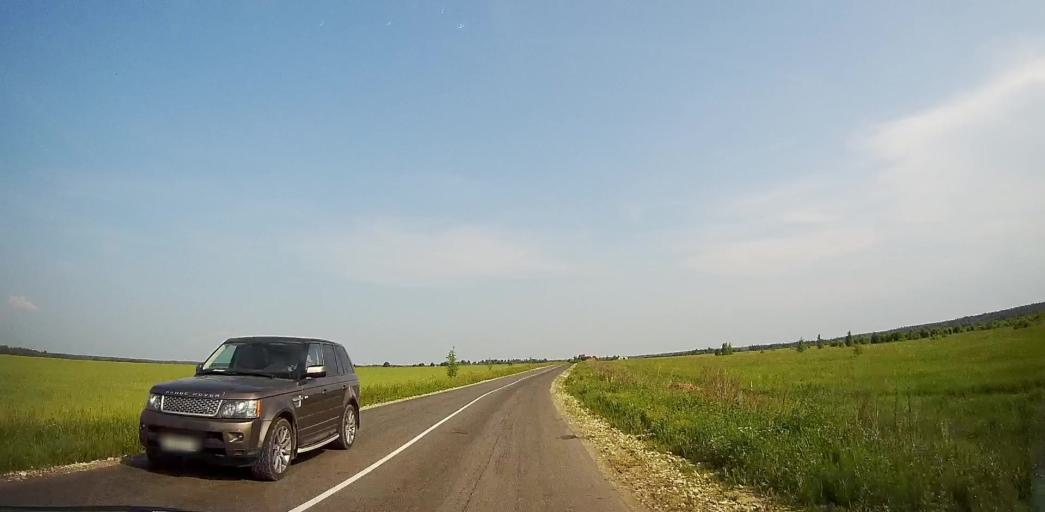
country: RU
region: Moskovskaya
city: Yakovlevskoye
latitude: 55.4308
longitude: 37.9416
